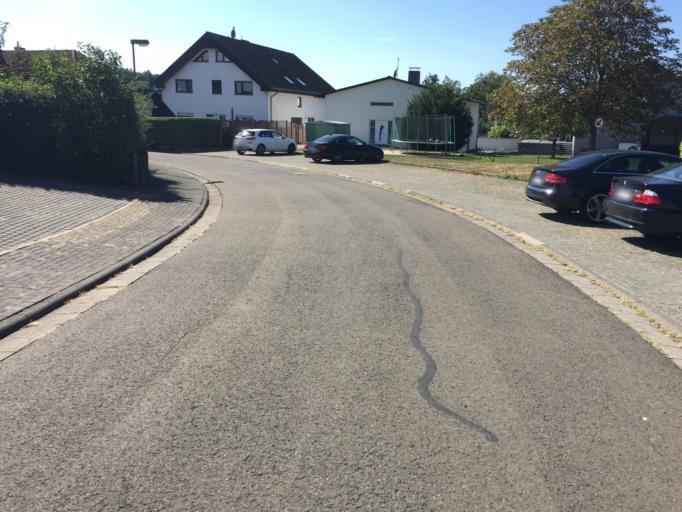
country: DE
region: Hesse
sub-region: Regierungsbezirk Giessen
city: Reiskirchen
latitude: 50.5921
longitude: 8.8833
